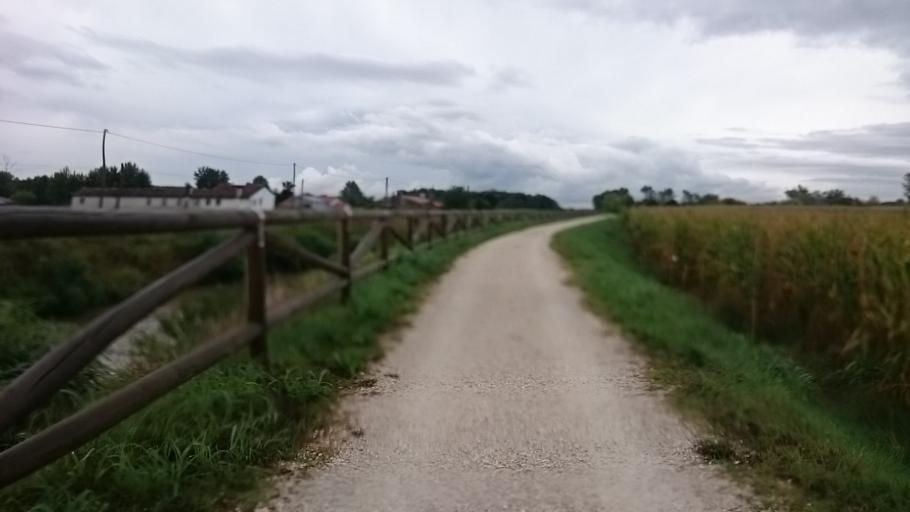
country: IT
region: Veneto
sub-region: Provincia di Padova
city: Loreggiola
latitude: 45.6260
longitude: 11.9262
